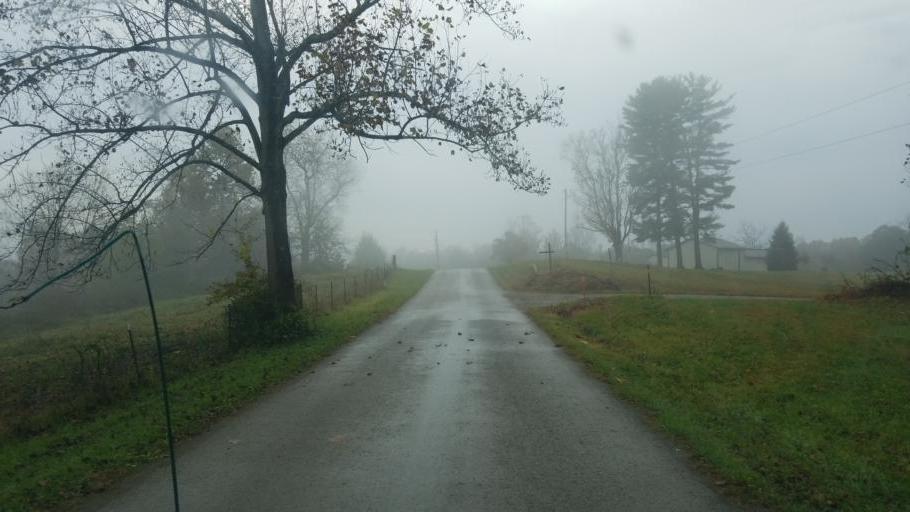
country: US
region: Ohio
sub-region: Morgan County
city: McConnelsville
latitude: 39.5012
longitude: -81.8214
